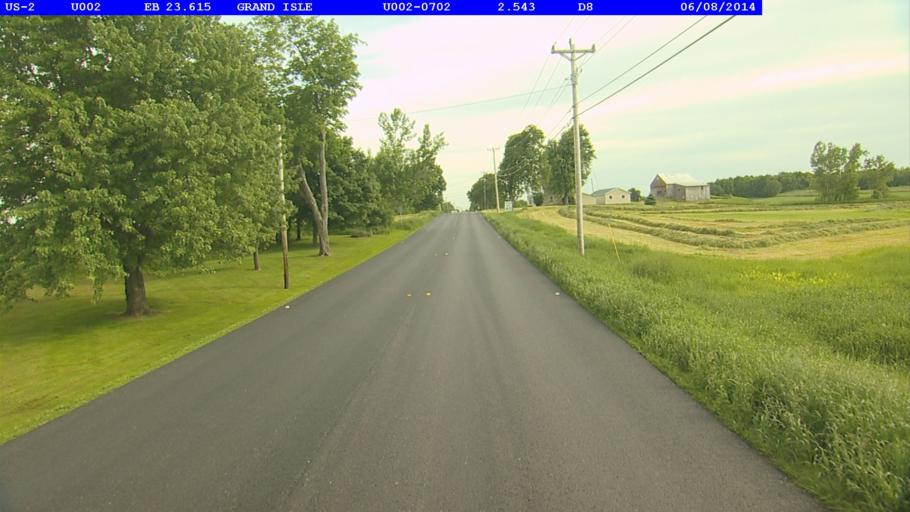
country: US
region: Vermont
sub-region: Grand Isle County
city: North Hero
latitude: 44.7308
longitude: -73.2916
